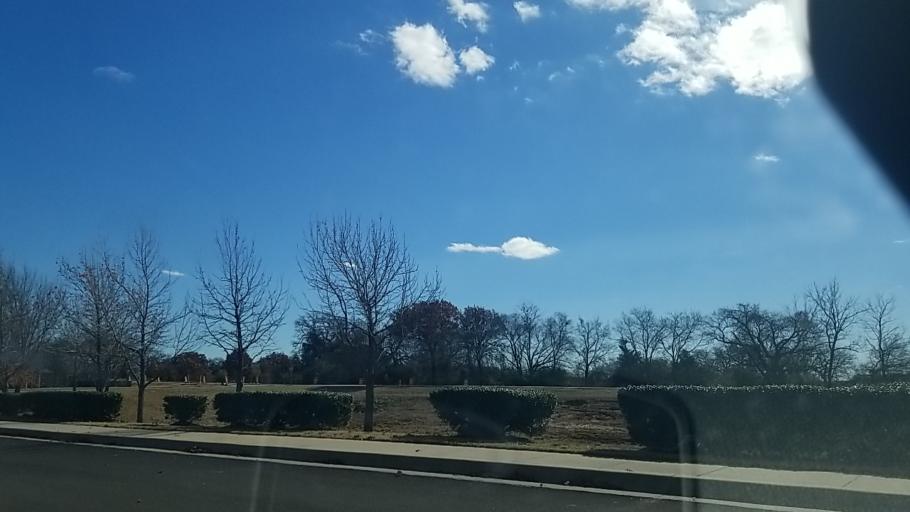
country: US
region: Texas
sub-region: Denton County
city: Denton
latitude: 33.1957
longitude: -97.0897
